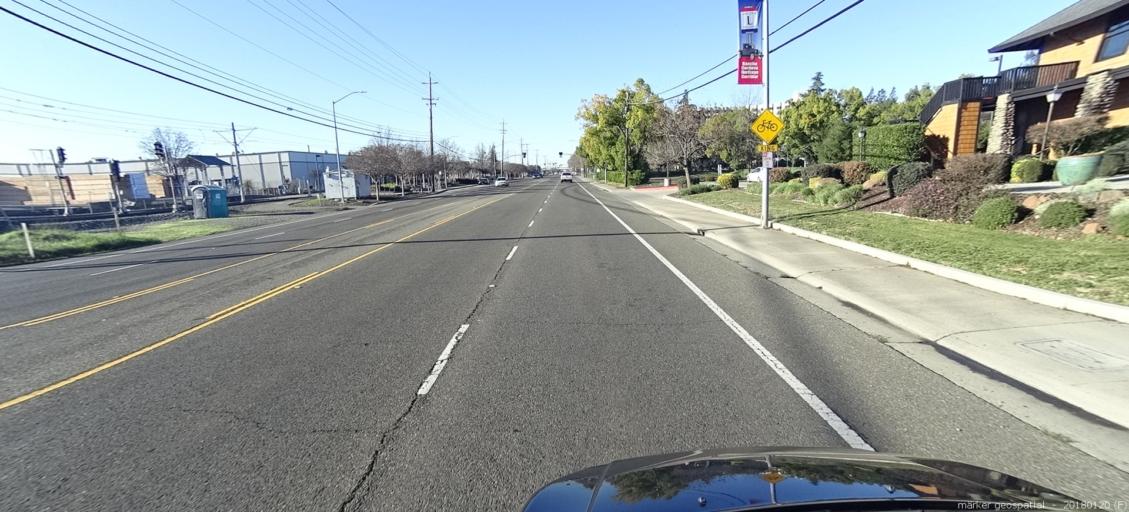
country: US
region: California
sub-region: Sacramento County
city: Gold River
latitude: 38.6076
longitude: -121.2657
